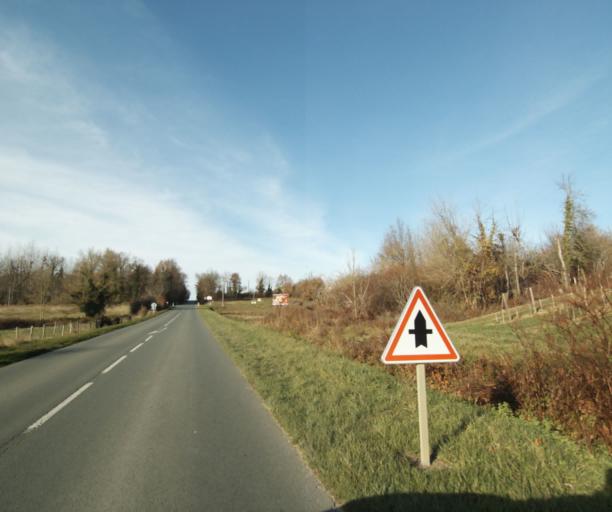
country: FR
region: Poitou-Charentes
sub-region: Departement de la Charente-Maritime
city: Burie
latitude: 45.7966
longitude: -0.4422
